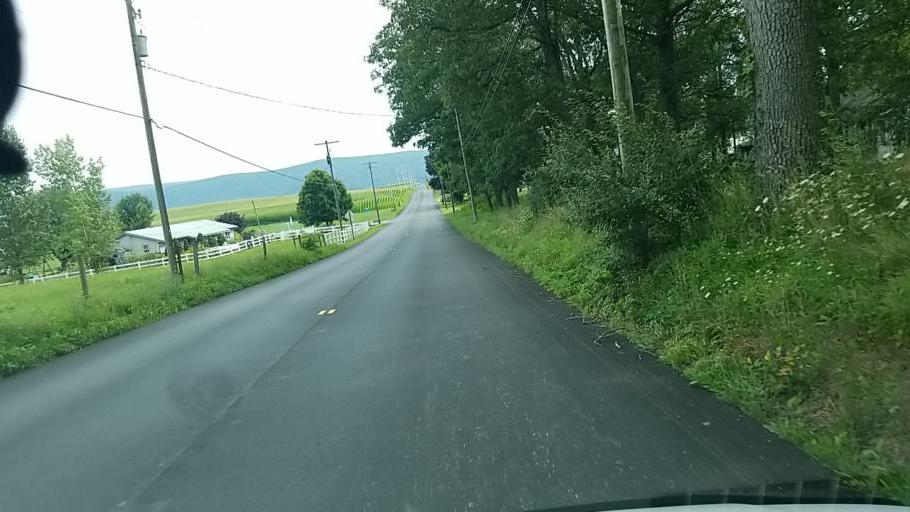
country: US
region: Pennsylvania
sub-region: Dauphin County
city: Elizabethville
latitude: 40.5817
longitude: -76.8156
